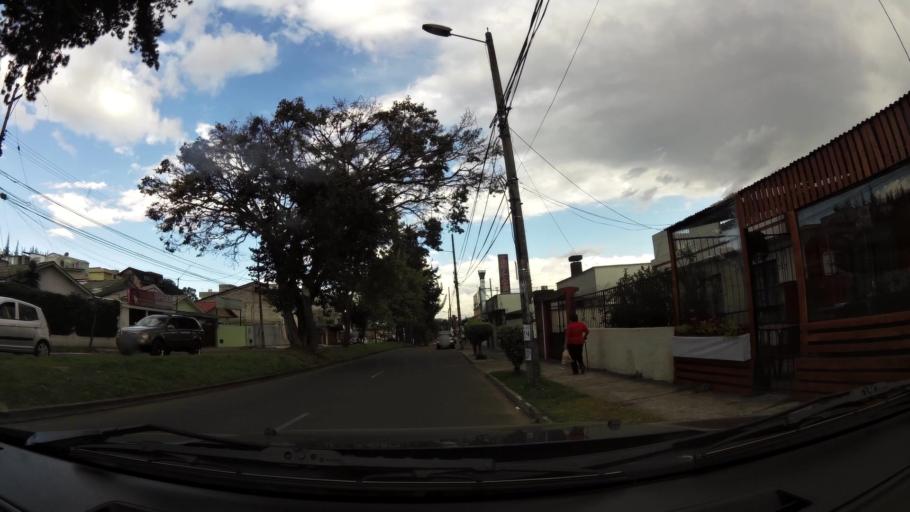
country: EC
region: Pichincha
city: Quito
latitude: -0.1356
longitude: -78.4866
